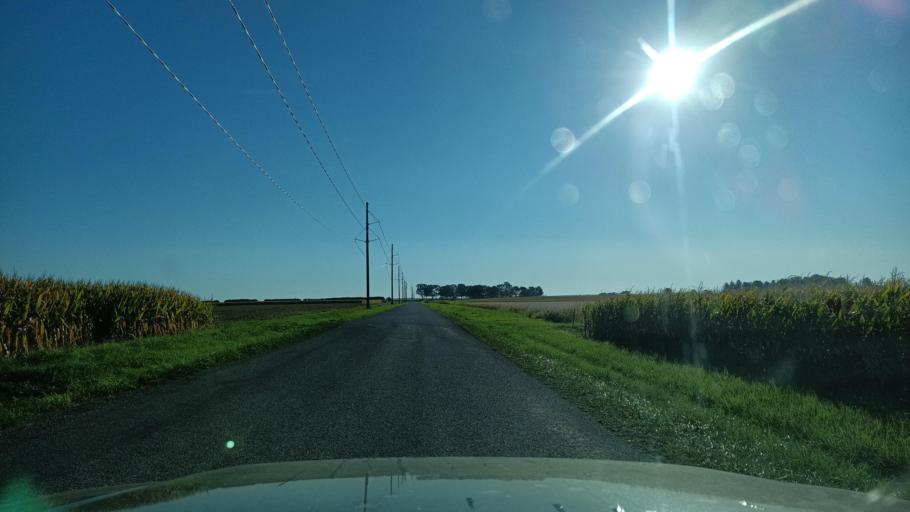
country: US
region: Illinois
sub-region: Champaign County
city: Savoy
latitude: 40.0546
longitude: -88.2001
